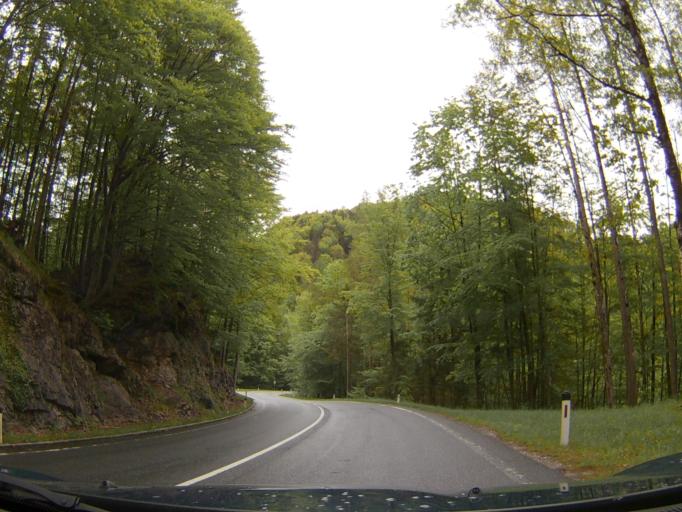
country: AT
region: Salzburg
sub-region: Politischer Bezirk Salzburg-Umgebung
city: Sankt Gilgen
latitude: 47.7896
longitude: 13.3901
